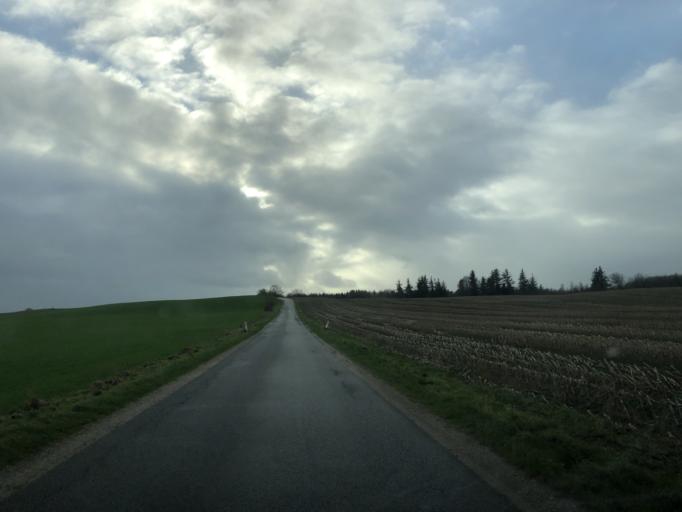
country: DK
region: North Denmark
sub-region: Rebild Kommune
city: Stovring
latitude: 56.9155
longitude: 9.7809
